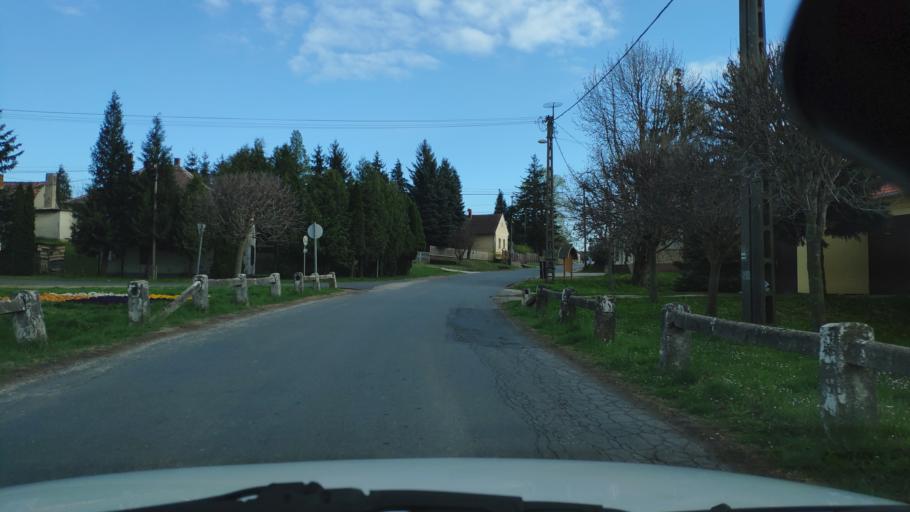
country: HU
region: Zala
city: Zalakomar
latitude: 46.4872
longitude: 17.1297
